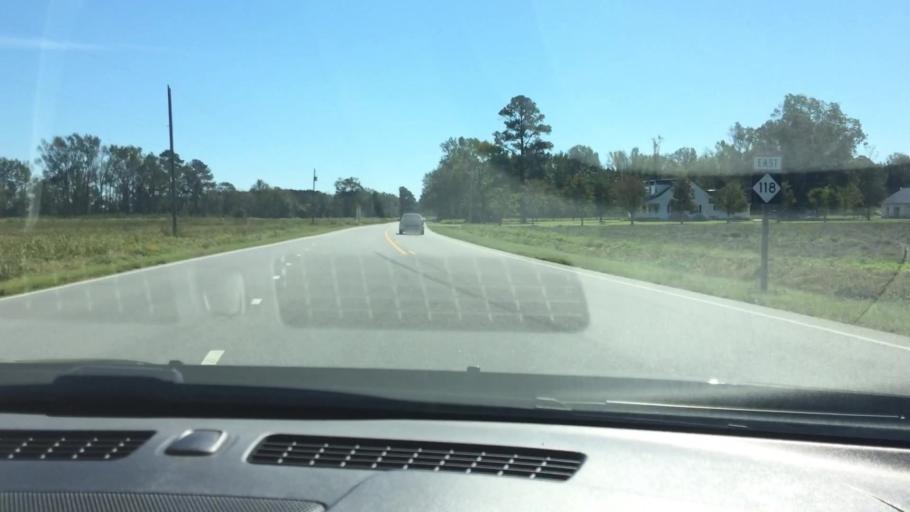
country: US
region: North Carolina
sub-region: Pitt County
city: Grifton
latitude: 35.3612
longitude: -77.3456
